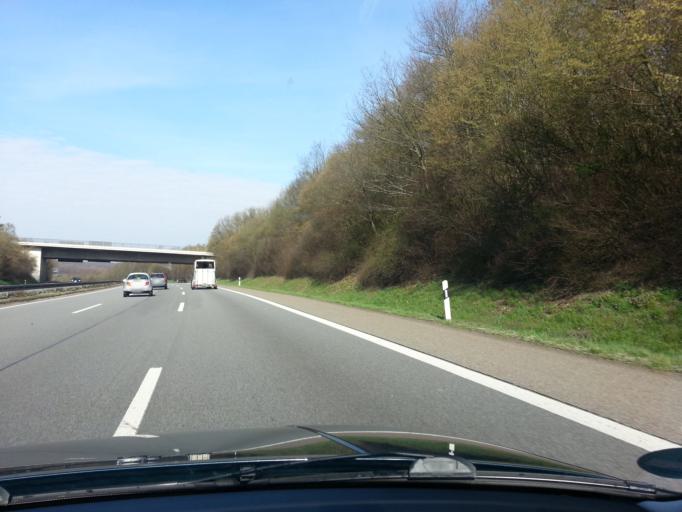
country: DE
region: Saarland
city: Spiesen-Elversberg
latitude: 49.3230
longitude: 7.1365
